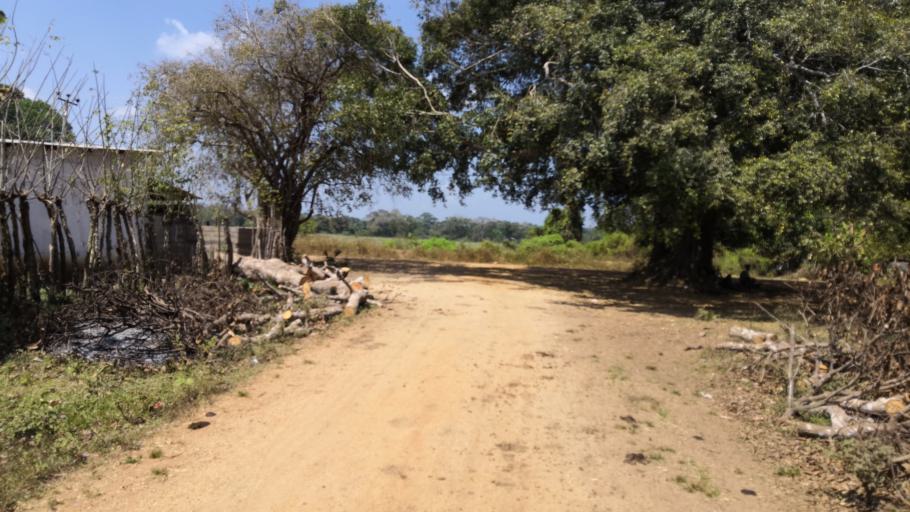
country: LK
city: Padaviya Divisional Secretariat
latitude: 8.9706
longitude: 80.6765
